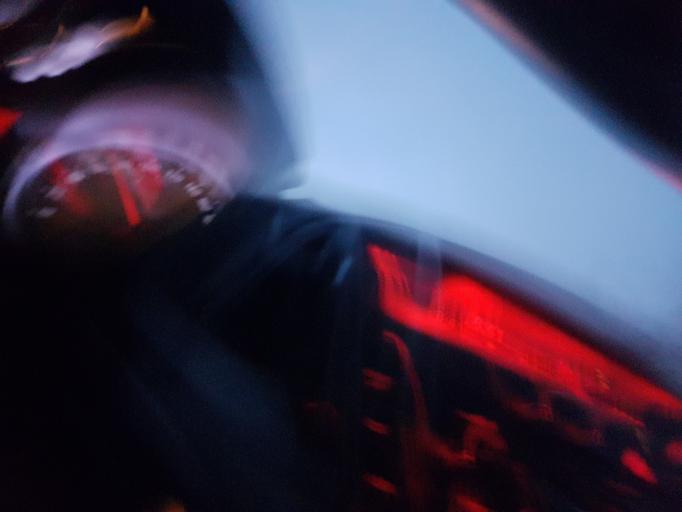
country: RU
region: Moskovskaya
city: Istra
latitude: 55.9072
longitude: 36.8831
